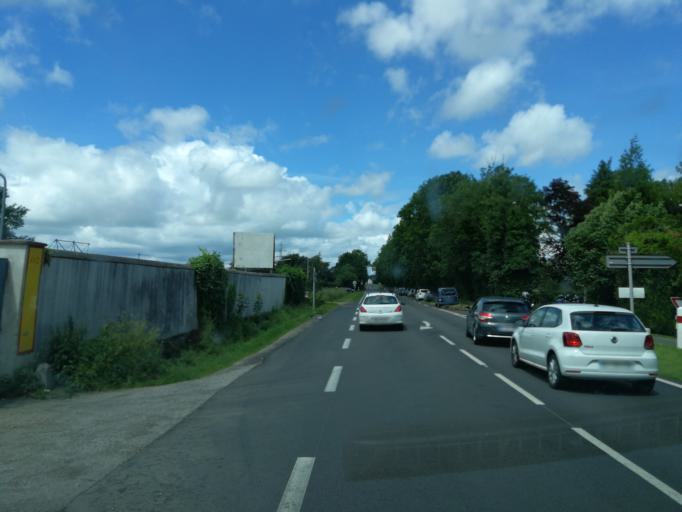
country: FR
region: Haute-Normandie
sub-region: Departement de la Seine-Maritime
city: Sahurs
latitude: 49.3499
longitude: 0.9239
